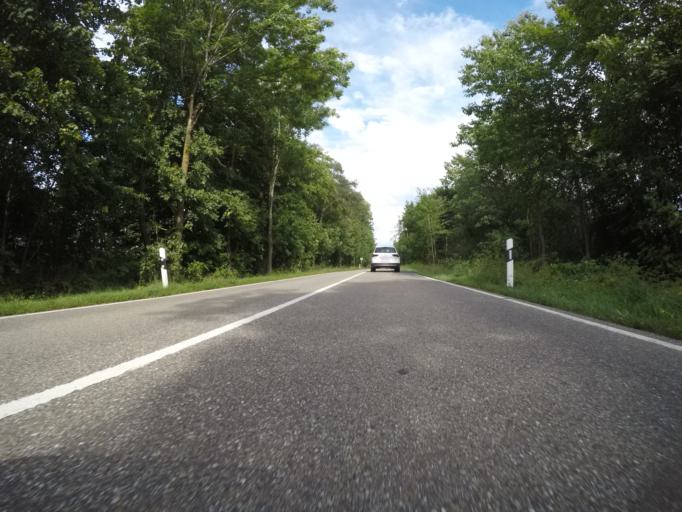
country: DE
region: Baden-Wuerttemberg
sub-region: Karlsruhe Region
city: Horb am Neckar
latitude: 48.4515
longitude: 8.6441
